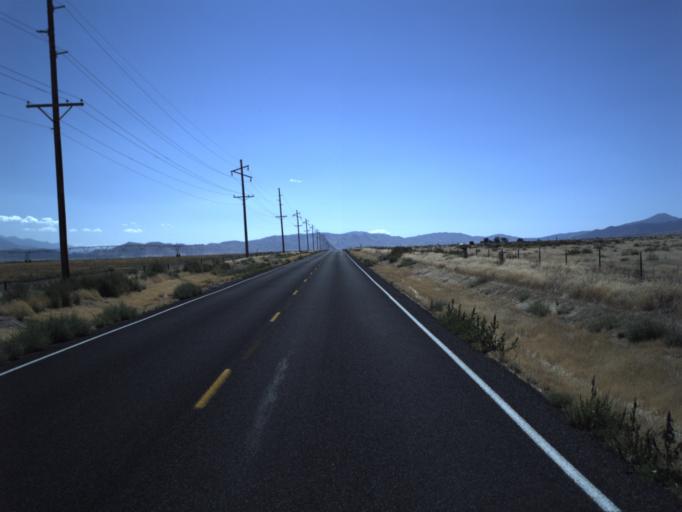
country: US
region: Utah
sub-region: Utah County
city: Genola
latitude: 40.0682
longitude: -111.9586
